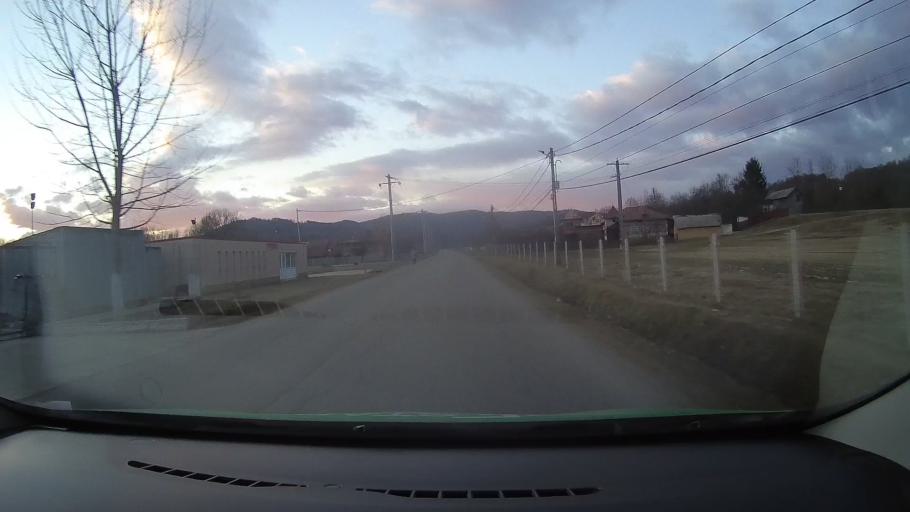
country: RO
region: Dambovita
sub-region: Comuna Valea Lunga
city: Valea Lunga-Cricov
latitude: 45.0634
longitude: 25.5881
